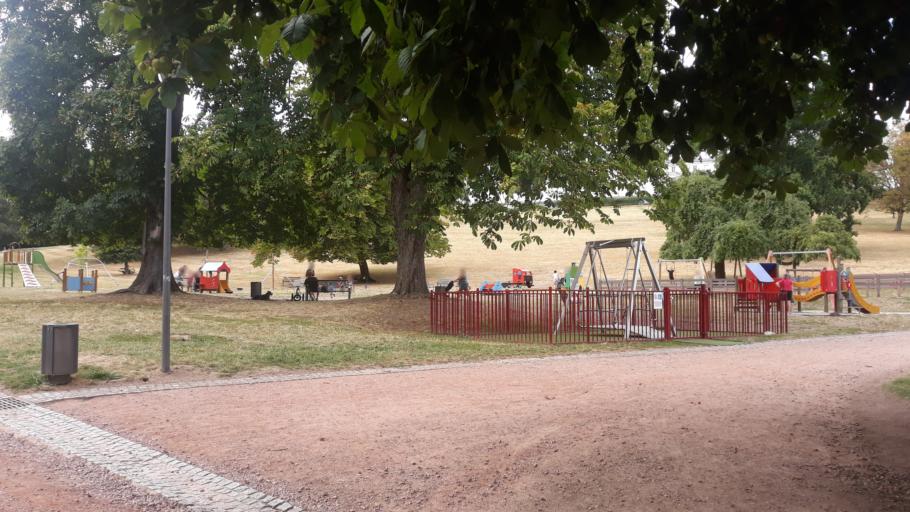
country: FR
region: Bourgogne
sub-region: Departement de Saone-et-Loire
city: Le Creusot
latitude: 46.8029
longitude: 4.4235
